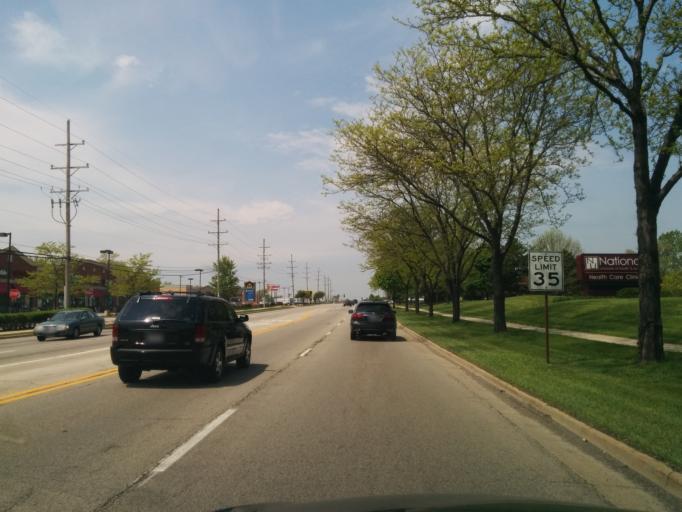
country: US
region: Illinois
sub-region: DuPage County
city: Lombard
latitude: 41.8603
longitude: -88.0127
